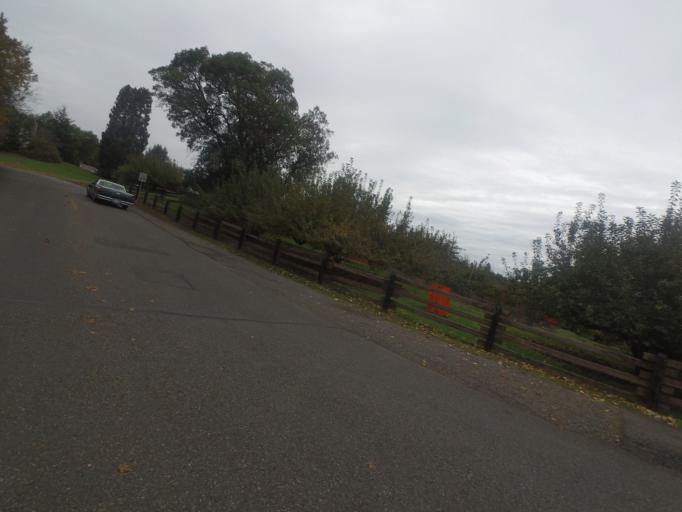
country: US
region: Washington
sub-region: Pierce County
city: University Place
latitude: 47.2201
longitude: -122.5615
